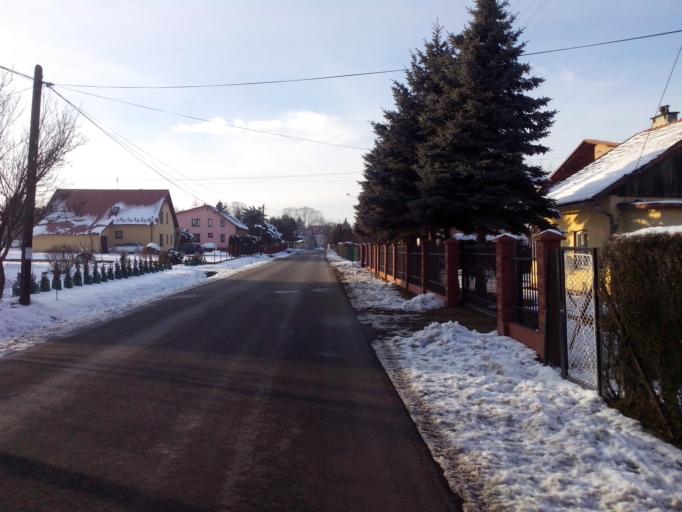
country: PL
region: Subcarpathian Voivodeship
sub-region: Powiat strzyzowski
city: Strzyzow
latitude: 49.8638
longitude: 21.8058
